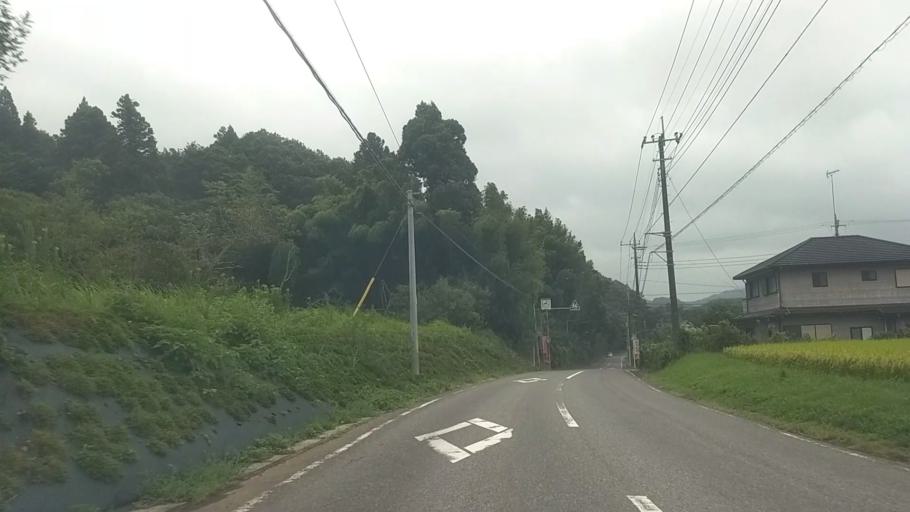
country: JP
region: Chiba
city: Kimitsu
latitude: 35.2349
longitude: 140.0041
